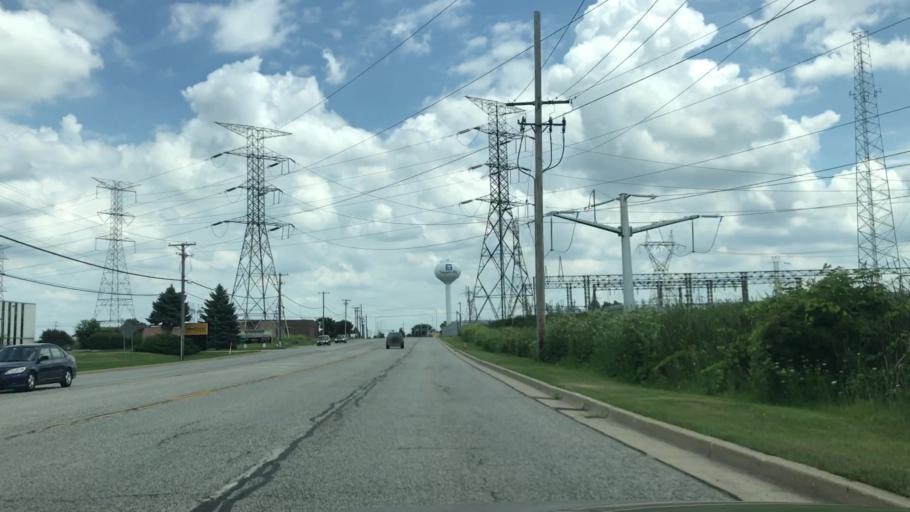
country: US
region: Illinois
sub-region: DuPage County
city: Warrenville
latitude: 41.7993
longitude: -88.2355
